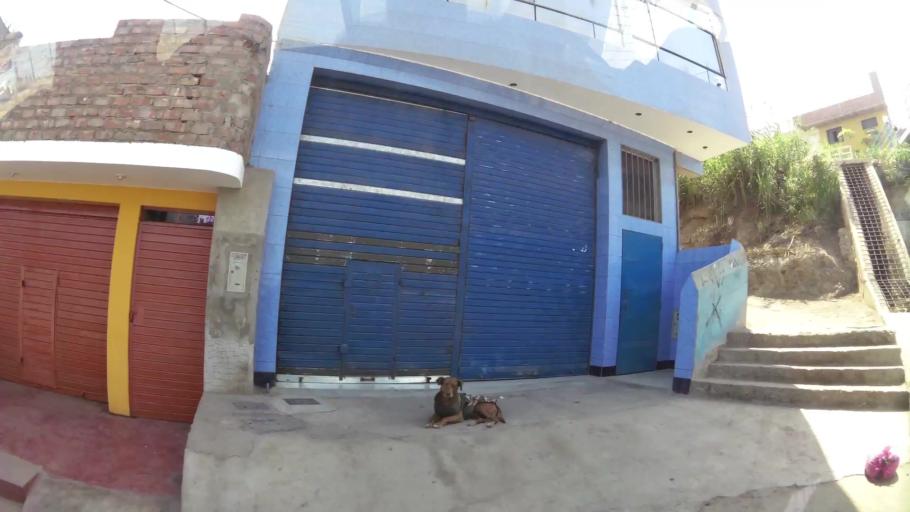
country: PE
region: Lima
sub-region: Provincia de Canete
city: Mala
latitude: -12.6585
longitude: -76.6291
